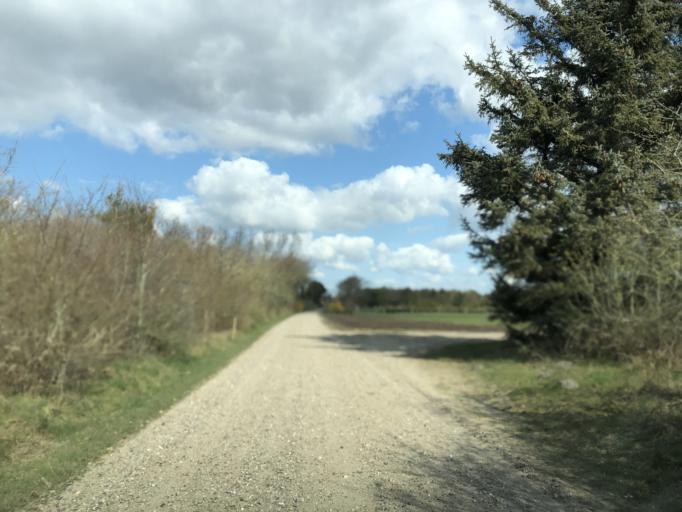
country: DK
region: Central Jutland
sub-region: Holstebro Kommune
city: Ulfborg
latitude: 56.3800
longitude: 8.2097
